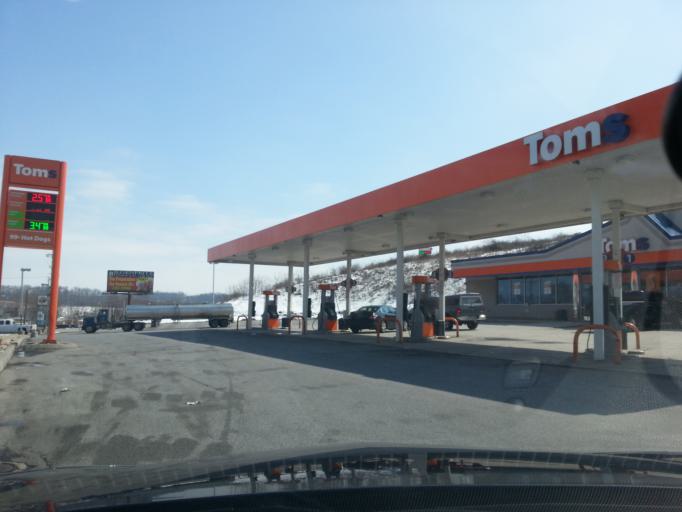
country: US
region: Pennsylvania
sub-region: York County
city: Shrewsbury
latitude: 39.7710
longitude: -76.6662
